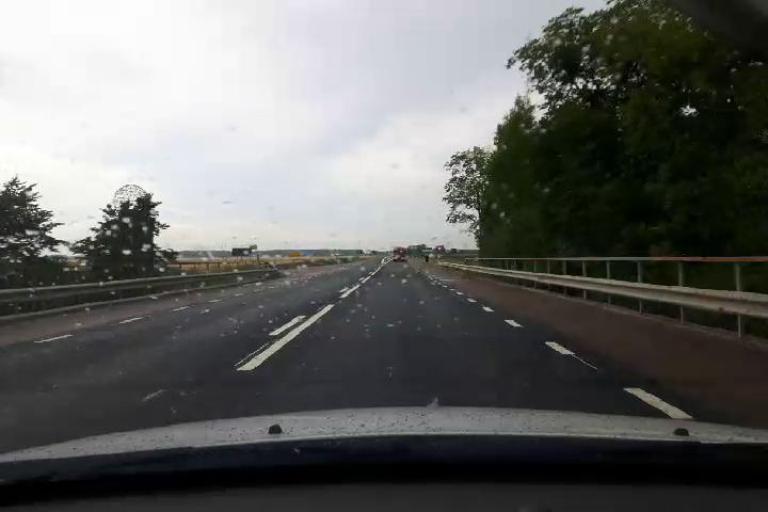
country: SE
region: Uppsala
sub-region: Osthammars Kommun
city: Bjorklinge
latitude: 59.9618
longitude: 17.5830
